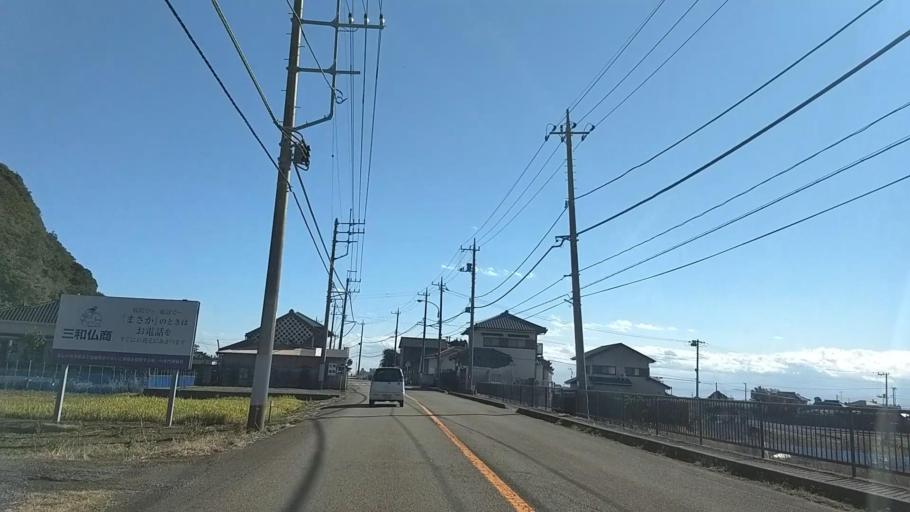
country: JP
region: Chiba
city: Tateyama
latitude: 34.9101
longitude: 139.8725
